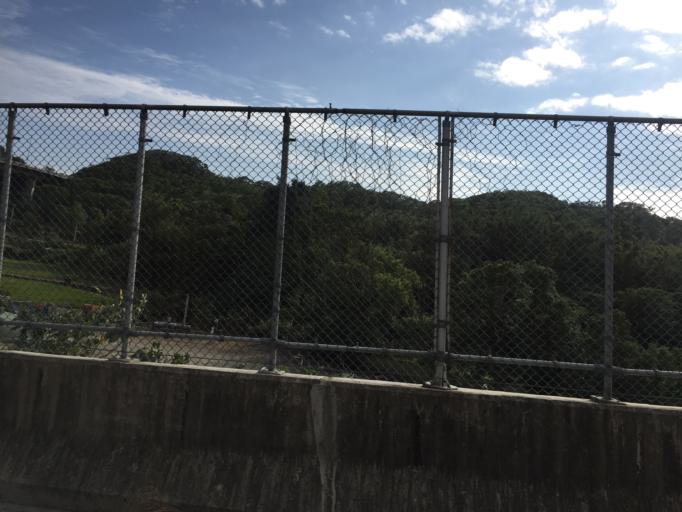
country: TW
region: Taiwan
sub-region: Hsinchu
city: Hsinchu
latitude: 24.7733
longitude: 120.9514
